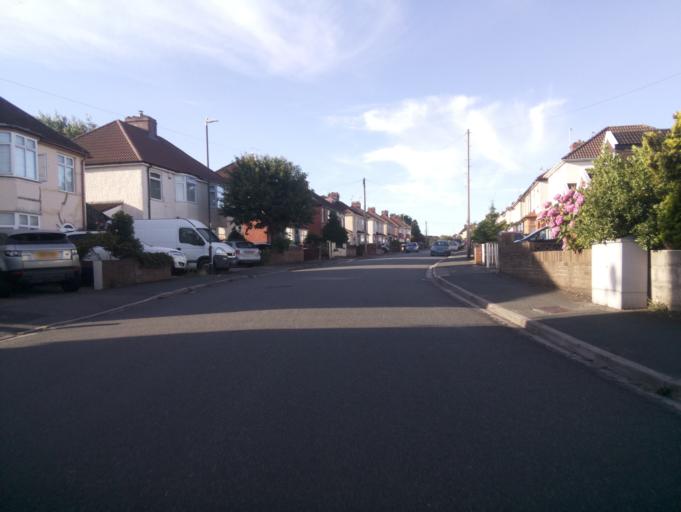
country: GB
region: England
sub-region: South Gloucestershire
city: Mangotsfield
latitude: 51.4860
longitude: -2.5006
